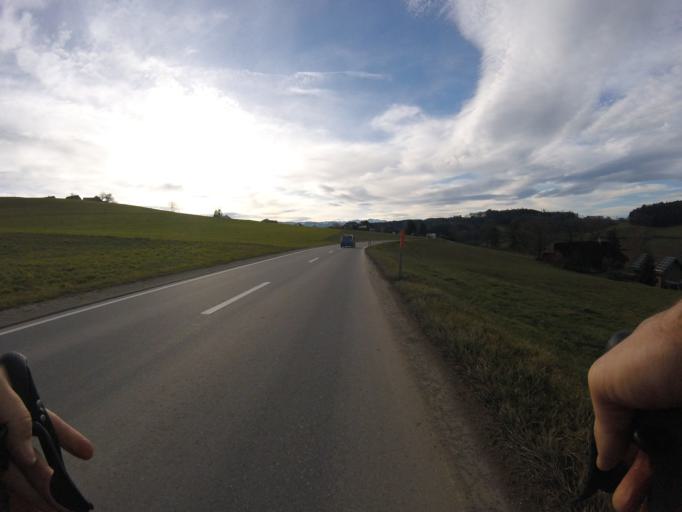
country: CH
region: Fribourg
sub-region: Sense District
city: Ueberstorf
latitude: 46.8564
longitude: 7.3162
